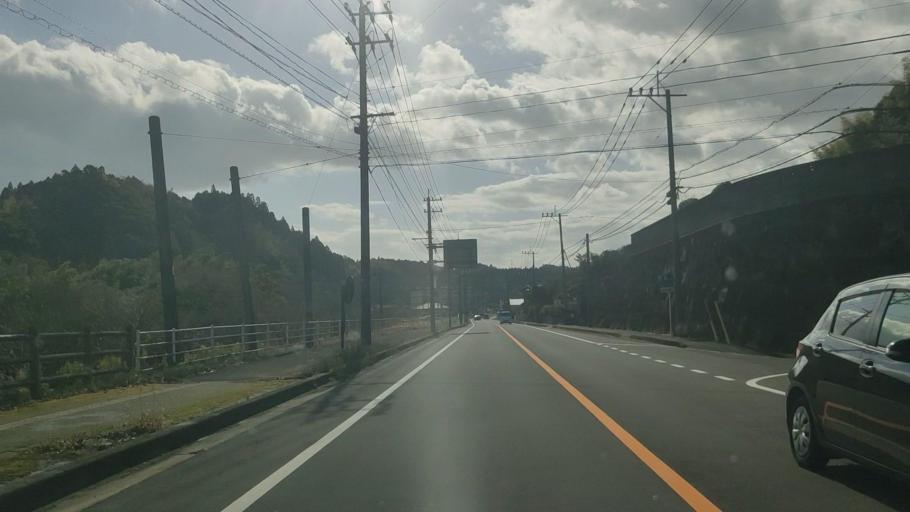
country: JP
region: Kagoshima
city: Okuchi-shinohara
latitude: 31.9453
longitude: 130.7111
